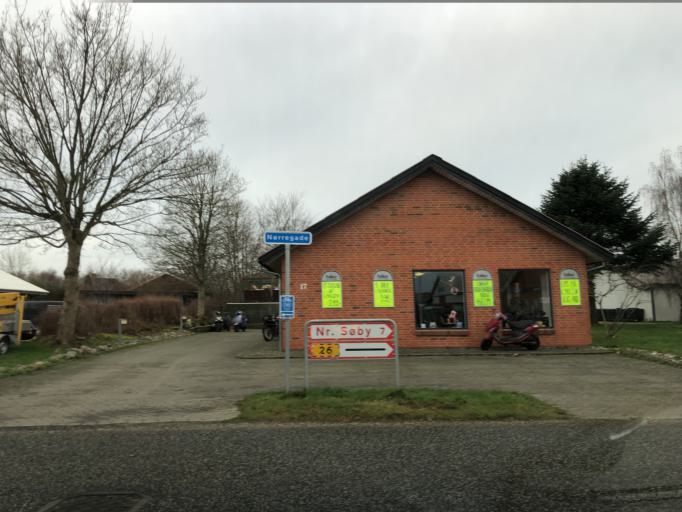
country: DK
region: Central Jutland
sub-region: Viborg Kommune
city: Stoholm
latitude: 56.4881
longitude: 9.1520
